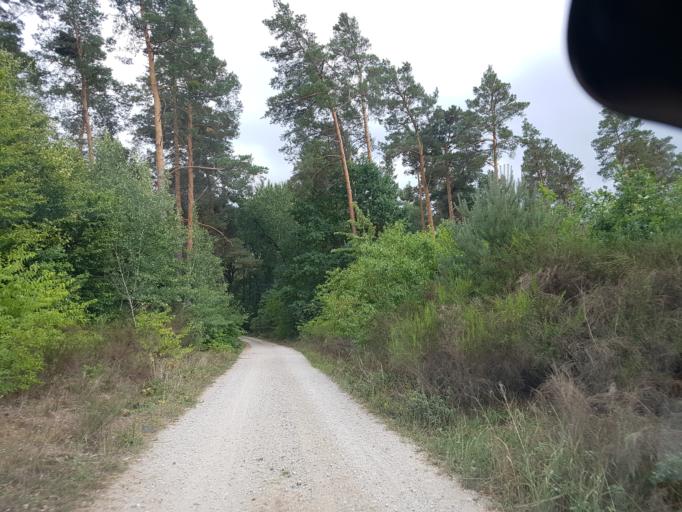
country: DE
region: Saxony-Anhalt
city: Rosslau
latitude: 52.0200
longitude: 12.2923
